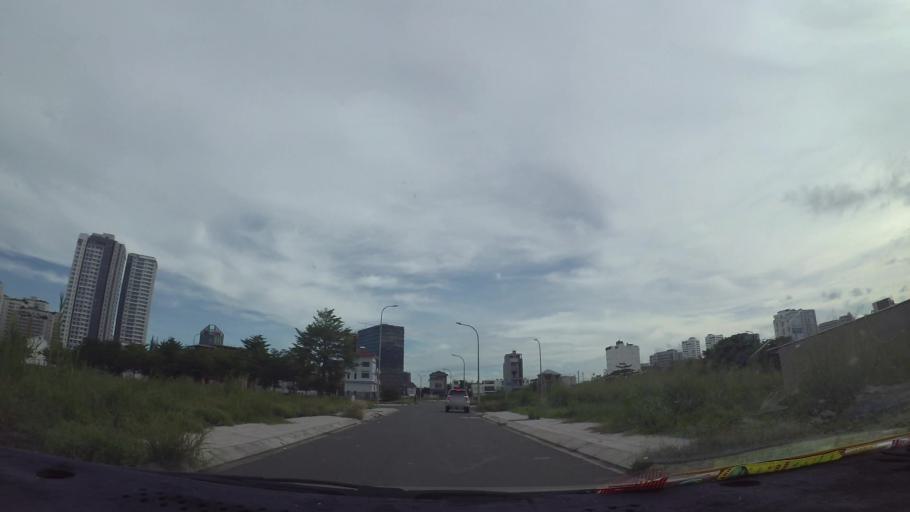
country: VN
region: Ho Chi Minh City
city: Quan Sau
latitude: 10.7472
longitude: 106.6580
